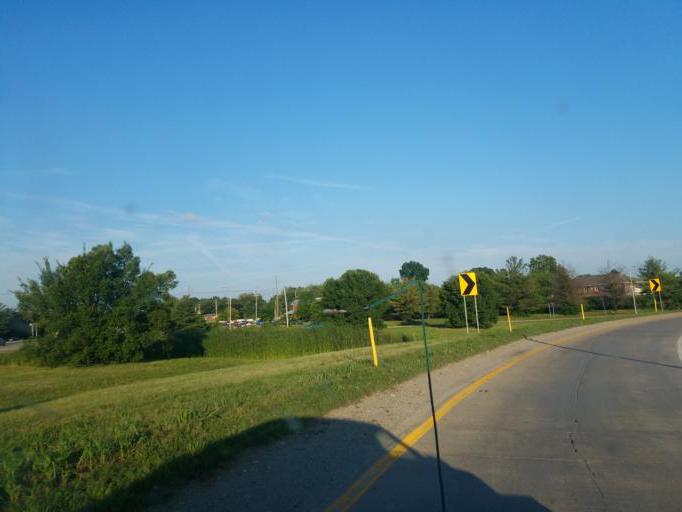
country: US
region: Kentucky
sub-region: Jefferson County
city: Okolona
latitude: 38.1365
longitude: -85.7033
